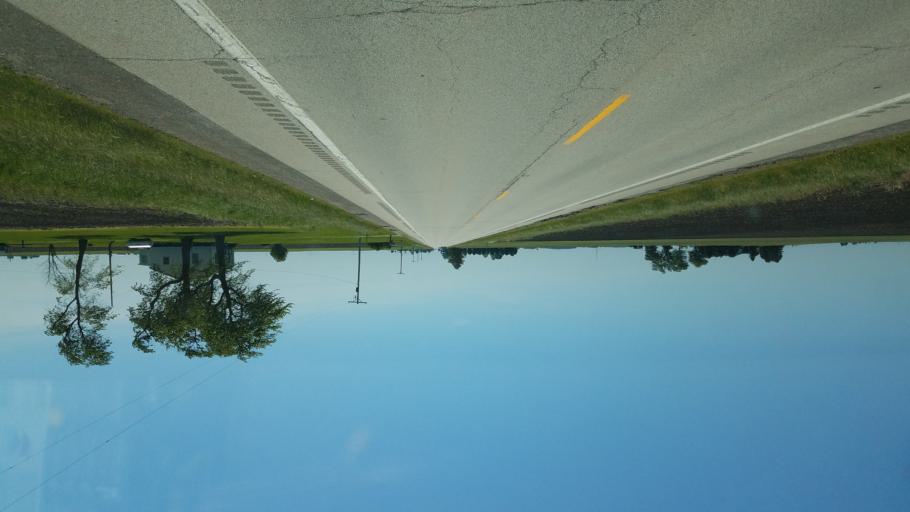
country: US
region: Illinois
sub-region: McLean County
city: Downs
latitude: 40.3122
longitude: -88.8737
